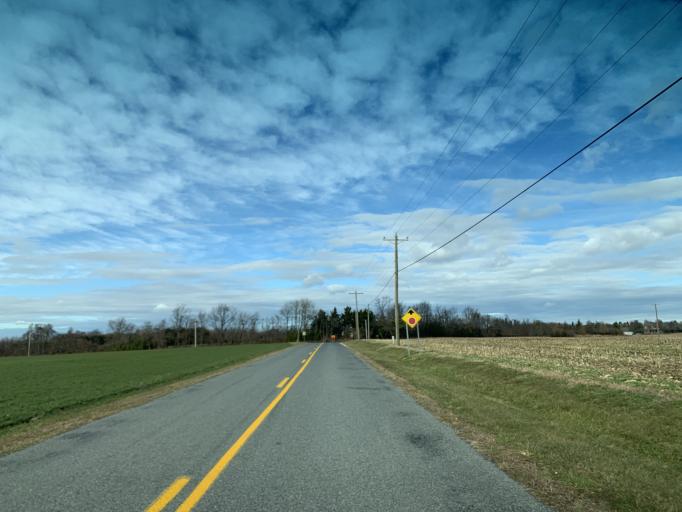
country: US
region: Maryland
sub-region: Kent County
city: Chestertown
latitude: 39.3479
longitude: -76.0543
